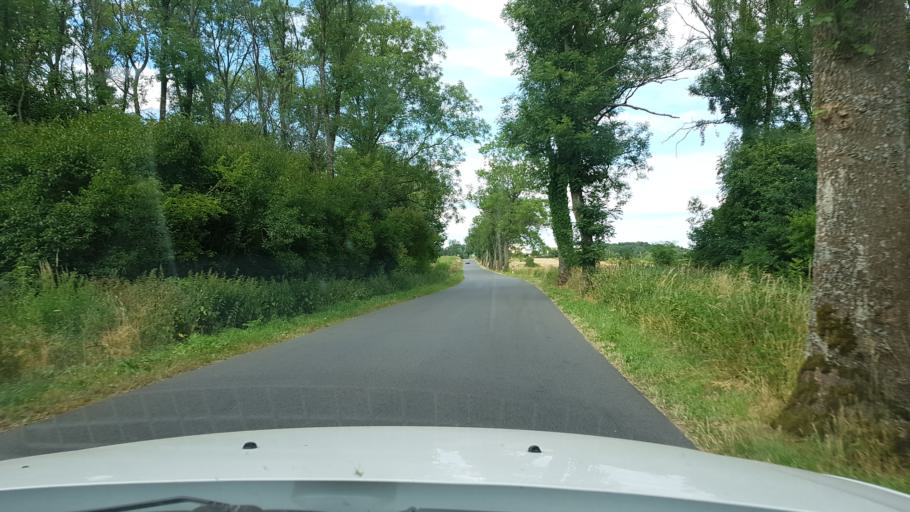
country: PL
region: West Pomeranian Voivodeship
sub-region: Powiat drawski
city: Kalisz Pomorski
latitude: 53.3280
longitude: 15.9273
